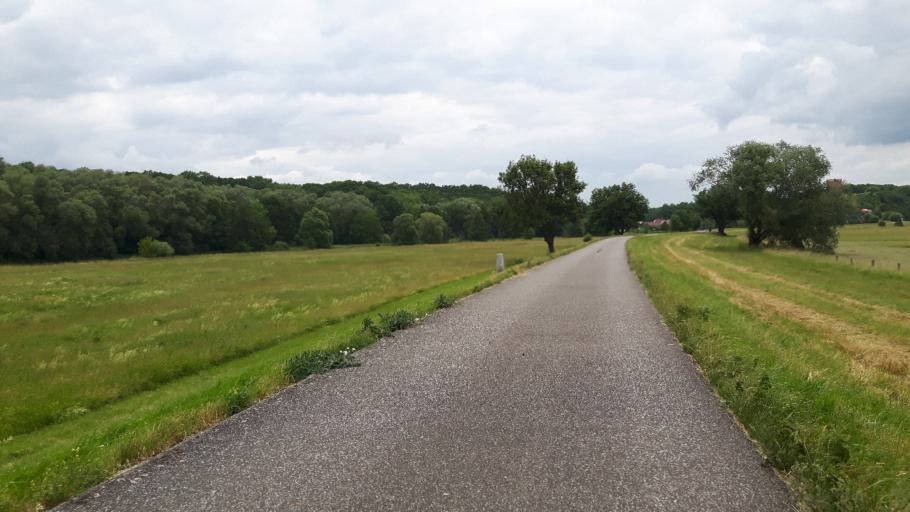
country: DE
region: Brandenburg
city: Schoneberg
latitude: 52.9711
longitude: 14.1124
